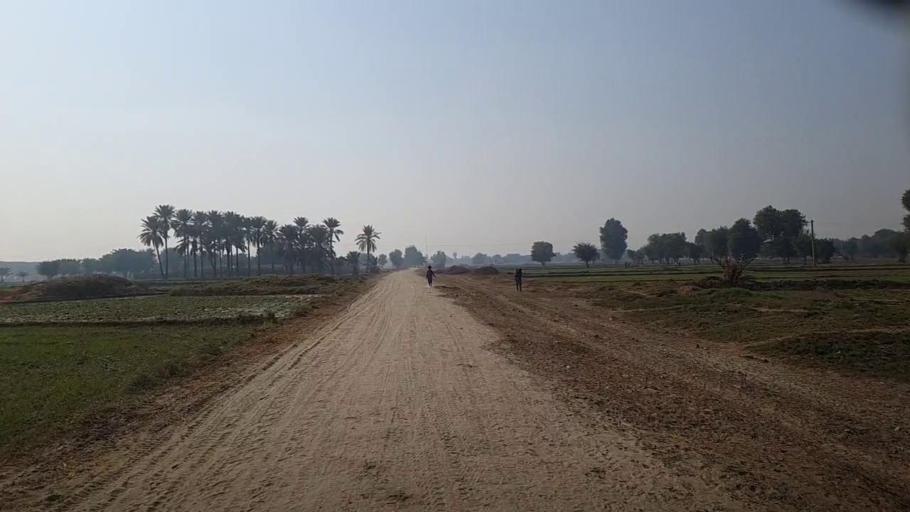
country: PK
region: Sindh
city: Bozdar
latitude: 27.2148
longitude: 68.5783
